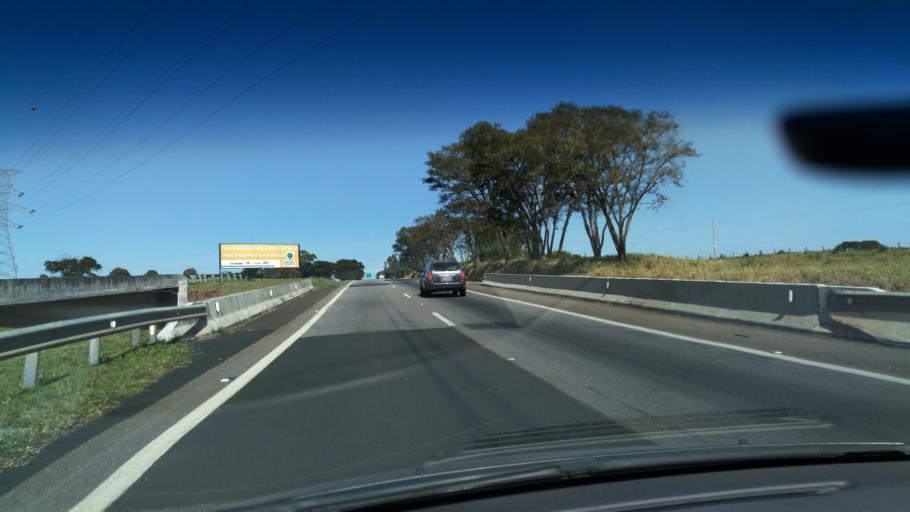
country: BR
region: Sao Paulo
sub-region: Mogi-Mirim
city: Mogi Mirim
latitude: -22.4580
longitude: -46.9824
